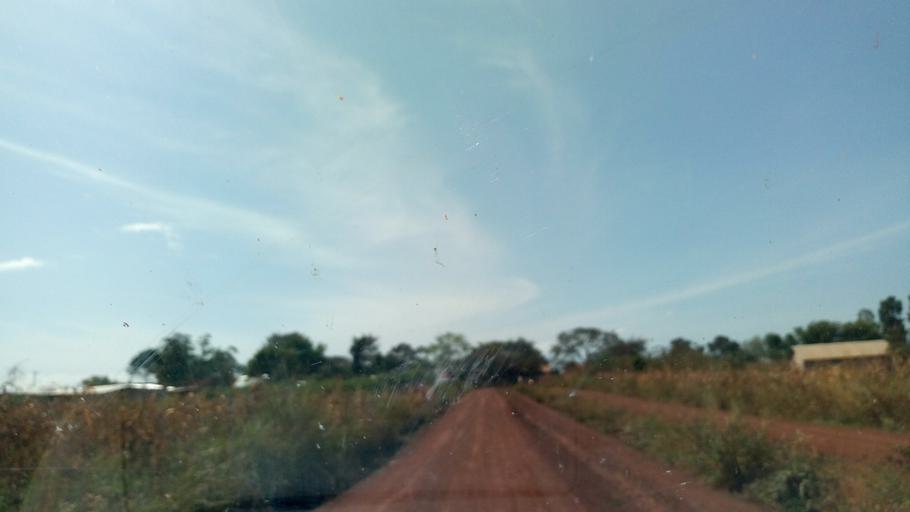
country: UG
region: Western Region
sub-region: Kiryandongo District
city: Kiryandongo
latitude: 1.9458
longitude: 32.1575
